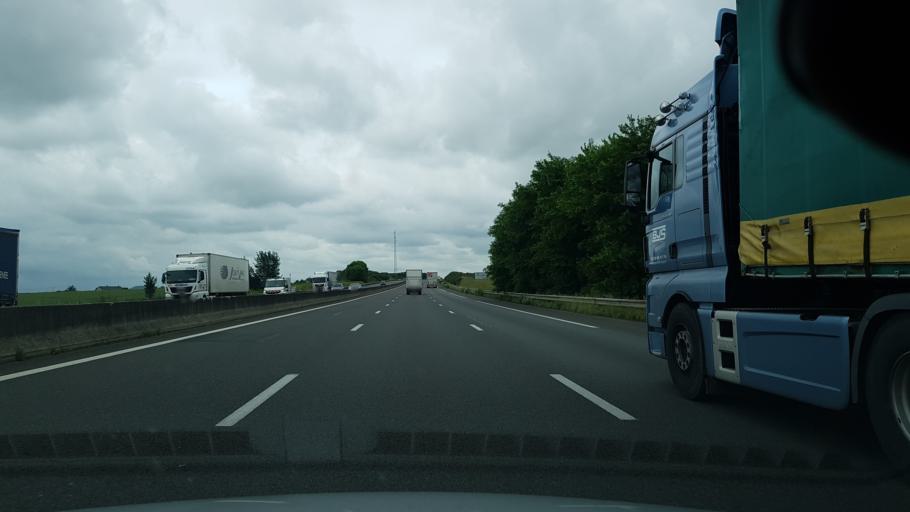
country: FR
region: Centre
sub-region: Departement d'Indre-et-Loire
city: Cangey
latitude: 47.5621
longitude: 1.0335
